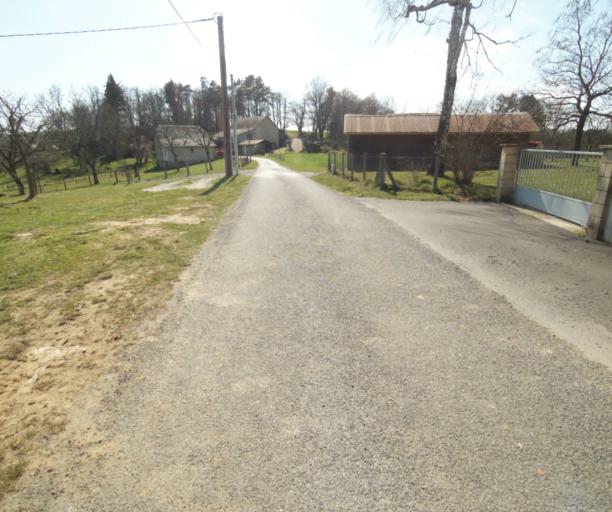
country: FR
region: Limousin
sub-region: Departement de la Correze
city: Saint-Mexant
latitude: 45.3041
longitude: 1.6476
